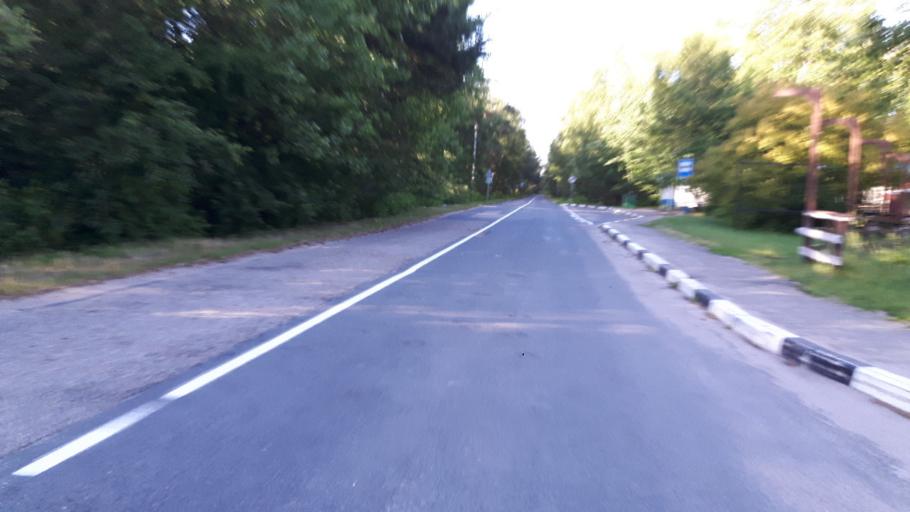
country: LT
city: Nida
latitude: 55.2371
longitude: 20.9101
